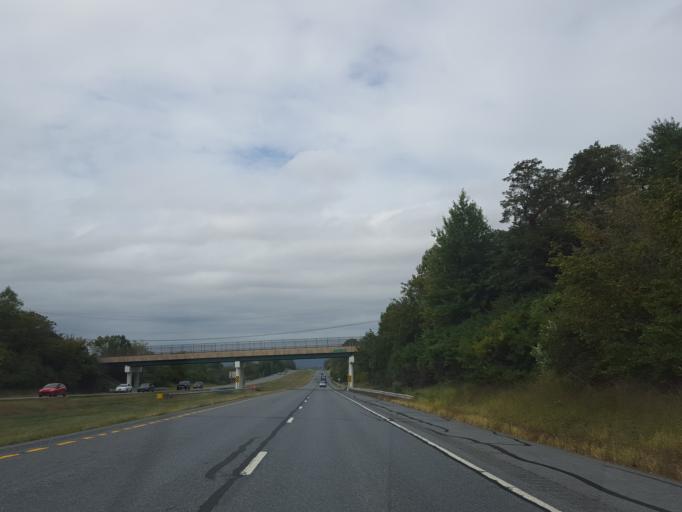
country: US
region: Maryland
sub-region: Frederick County
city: Jefferson
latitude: 39.3582
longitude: -77.5476
